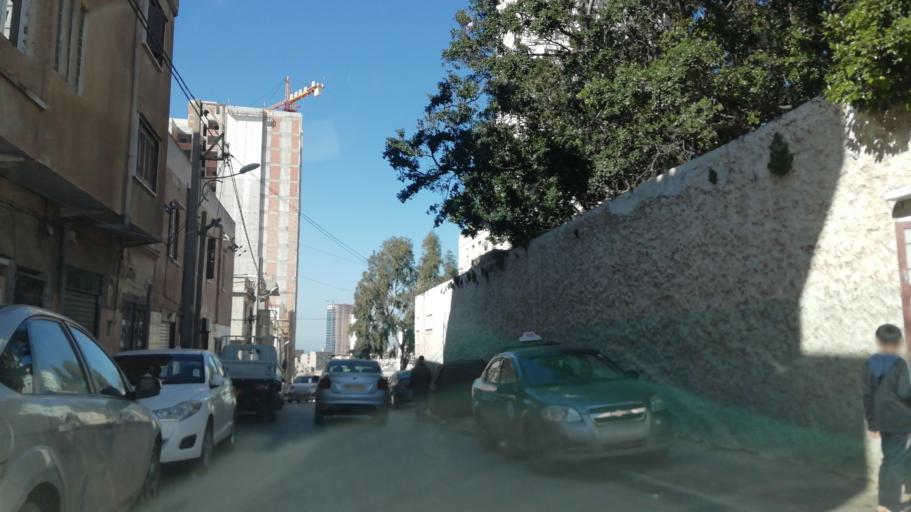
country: DZ
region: Oran
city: Oran
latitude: 35.7054
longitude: -0.6166
